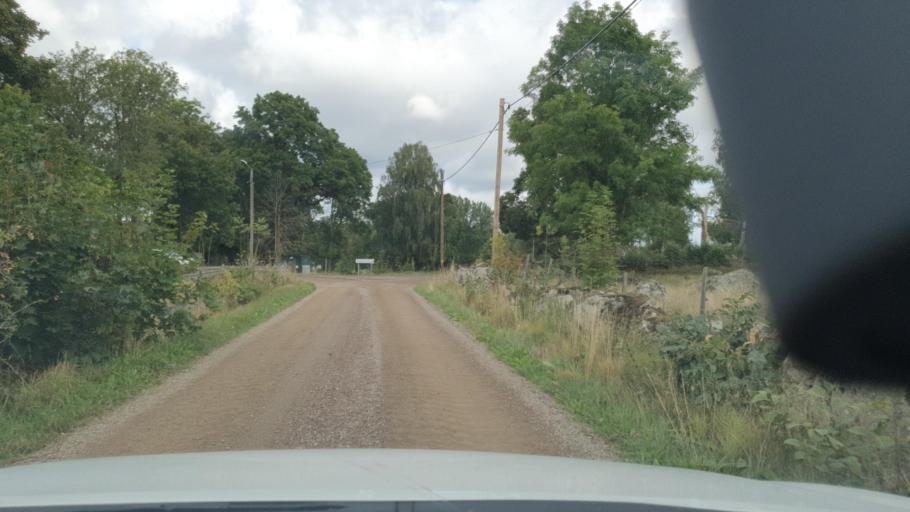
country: SE
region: Kalmar
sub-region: Hultsfreds Kommun
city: Malilla
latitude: 57.3240
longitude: 15.8097
